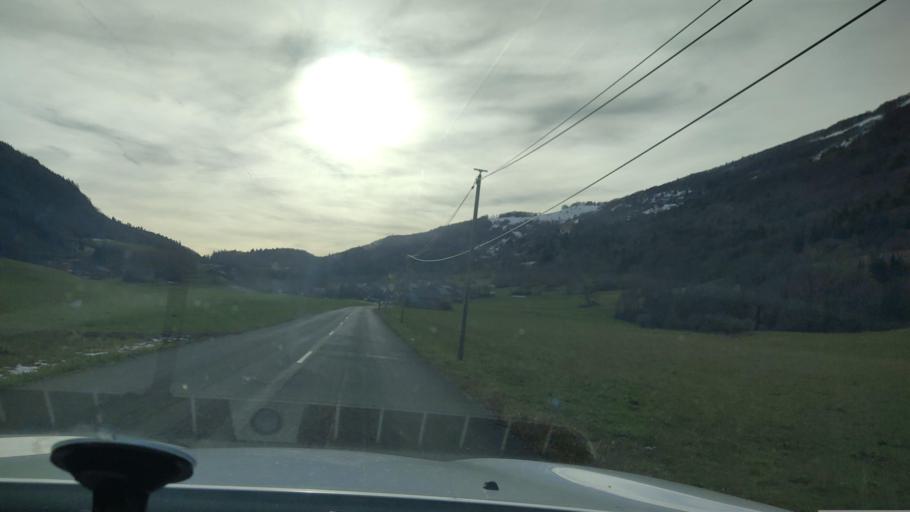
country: FR
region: Rhone-Alpes
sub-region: Departement de la Savoie
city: Coise-Saint-Jean-Pied-Gauthier
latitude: 45.6022
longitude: 6.1401
